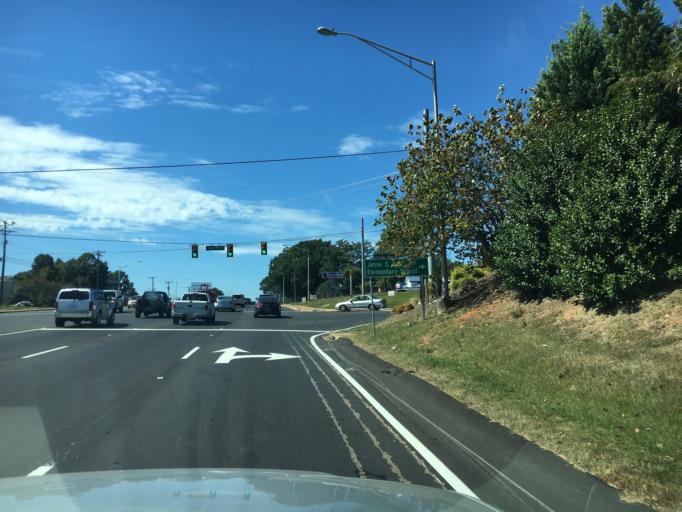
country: US
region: South Carolina
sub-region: Spartanburg County
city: Saxon
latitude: 34.9380
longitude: -81.9752
